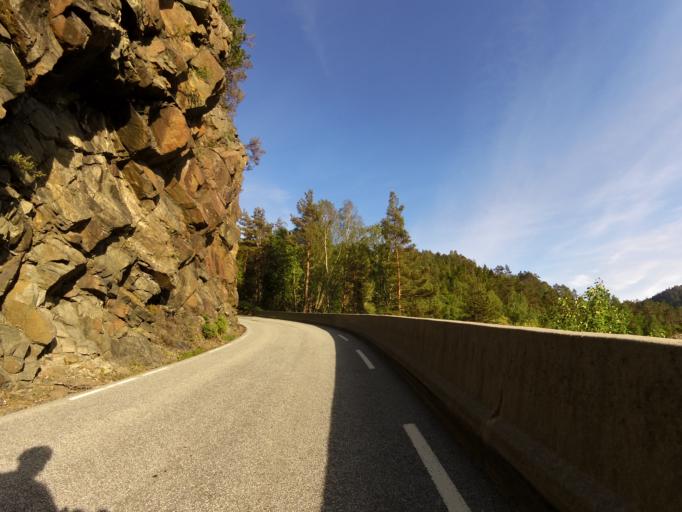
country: NO
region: Vest-Agder
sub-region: Flekkefjord
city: Flekkefjord
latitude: 58.2788
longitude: 6.6368
